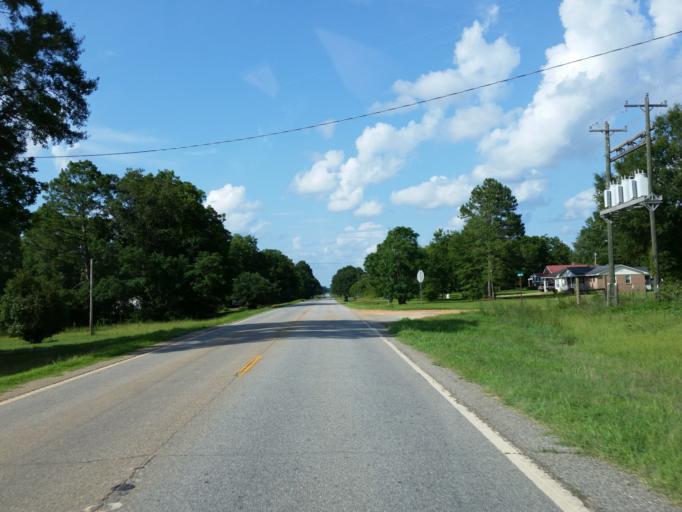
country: US
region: Georgia
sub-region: Lee County
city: Leesburg
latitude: 31.8221
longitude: -84.1081
